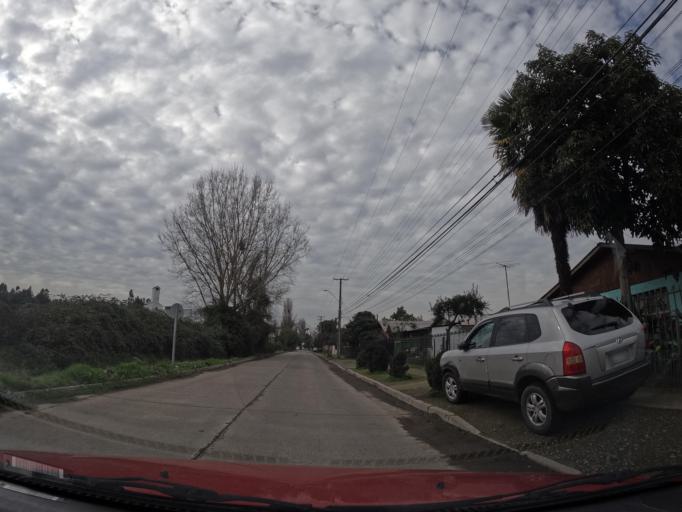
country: CL
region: Maule
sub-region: Provincia de Linares
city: Linares
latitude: -35.8544
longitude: -71.6126
